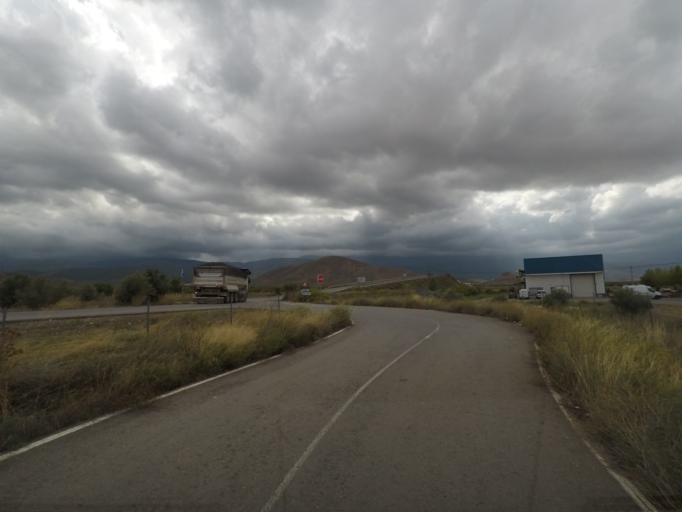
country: ES
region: Andalusia
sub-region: Provincia de Granada
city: Ferreira
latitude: 37.2058
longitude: -3.0463
